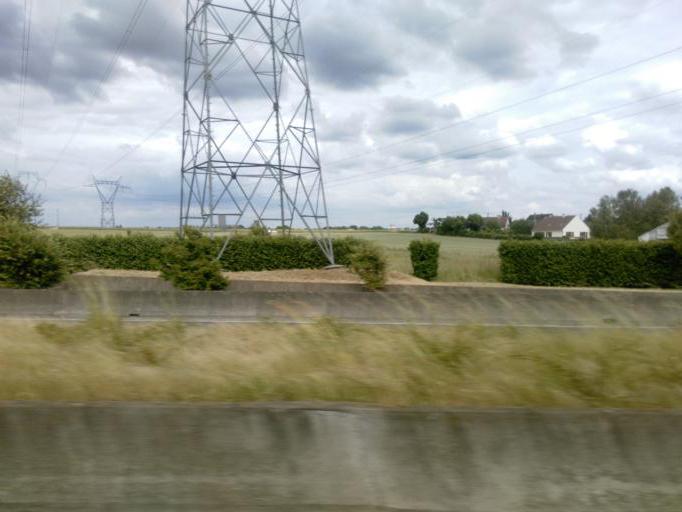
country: FR
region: Ile-de-France
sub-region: Departement du Val-d'Oise
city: Ennery
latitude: 49.0676
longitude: 2.0848
